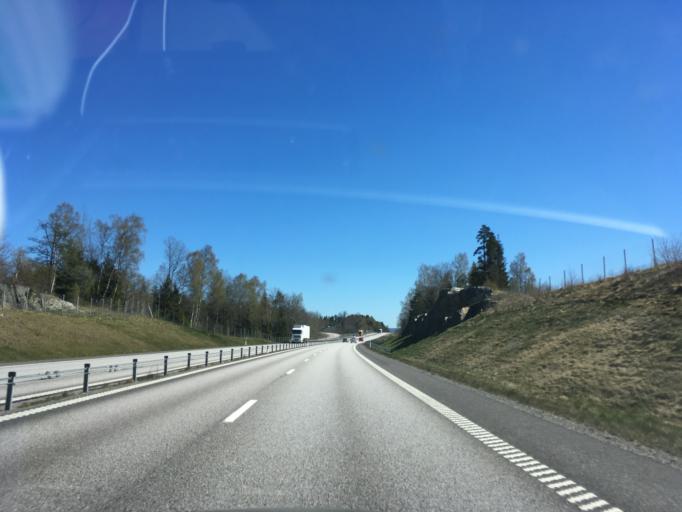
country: SE
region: Vaestra Goetaland
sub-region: Trollhattan
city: Sjuntorp
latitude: 58.2362
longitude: 12.2302
